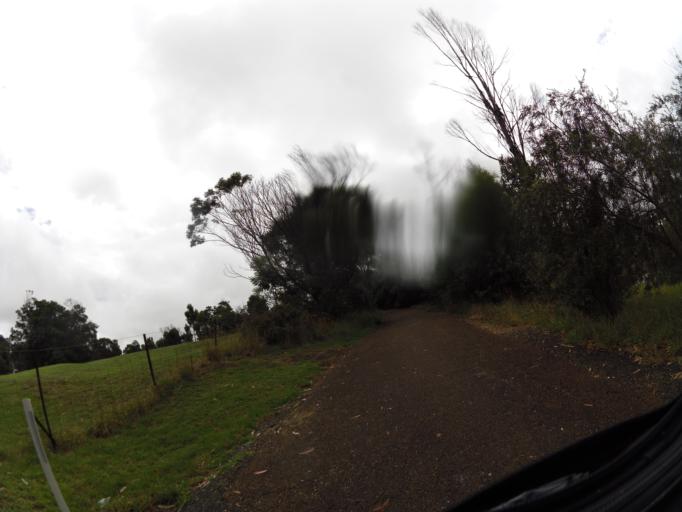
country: AU
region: Victoria
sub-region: East Gippsland
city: Bairnsdale
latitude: -37.8138
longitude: 147.7392
